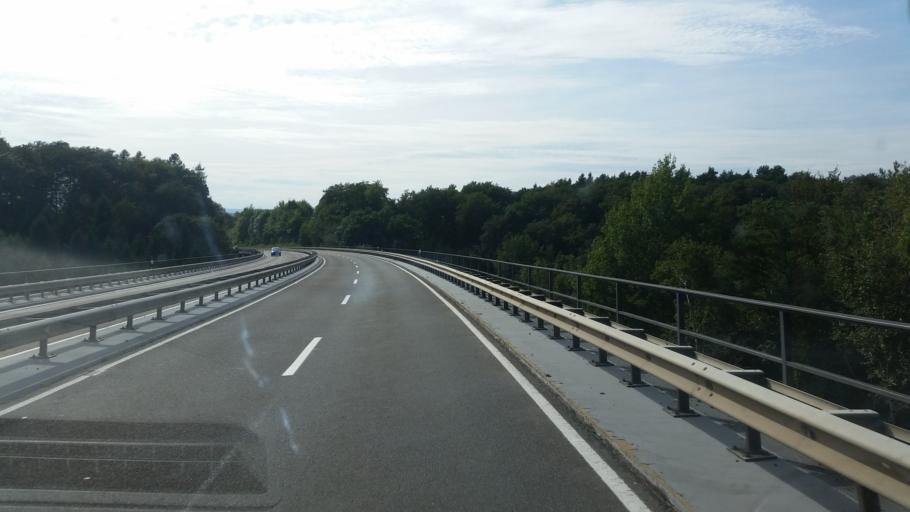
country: DE
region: Rheinland-Pfalz
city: Miellen
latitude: 50.3495
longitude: 7.6460
